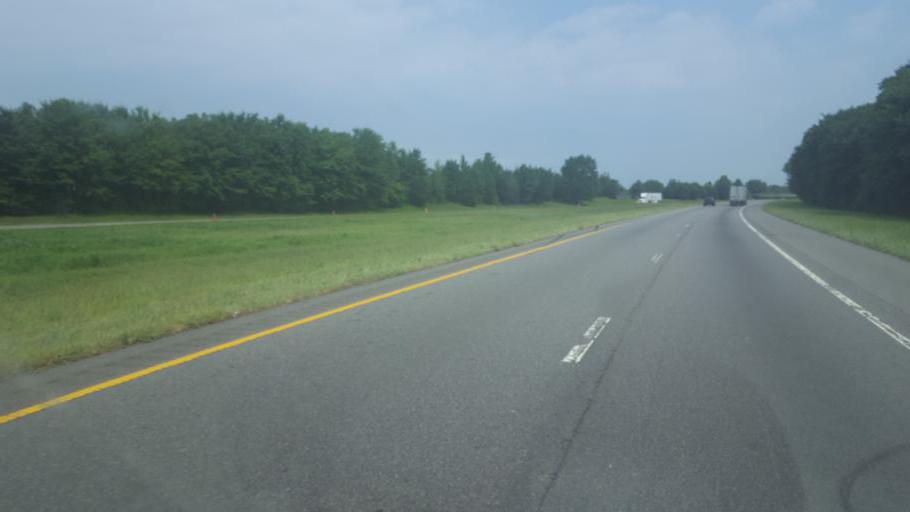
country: US
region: North Carolina
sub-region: Iredell County
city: Statesville
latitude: 35.9321
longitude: -80.8553
